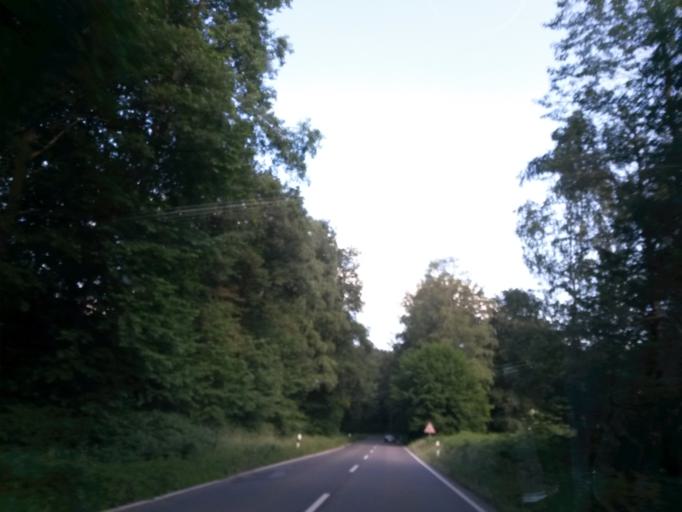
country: DE
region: North Rhine-Westphalia
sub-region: Regierungsbezirk Koln
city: Overath
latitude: 50.9202
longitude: 7.3220
